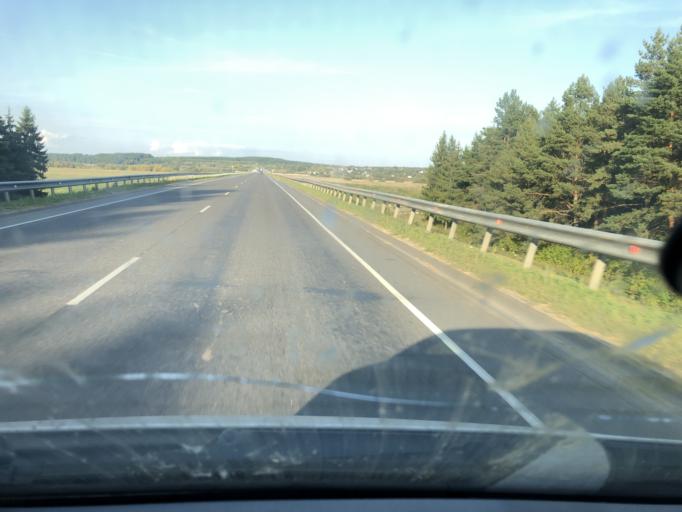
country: RU
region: Kaluga
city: Peremyshl'
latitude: 54.2841
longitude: 36.1566
